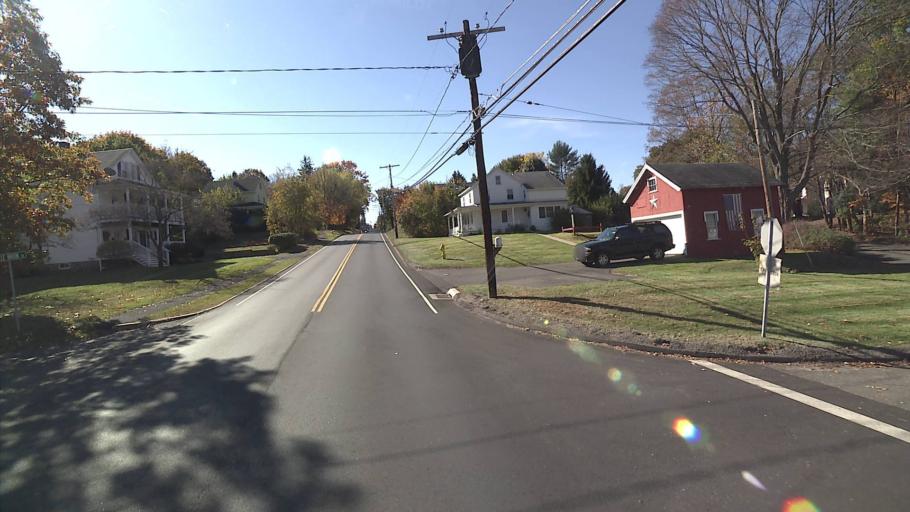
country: US
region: Connecticut
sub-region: Litchfield County
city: Watertown
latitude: 41.6093
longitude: -73.1162
